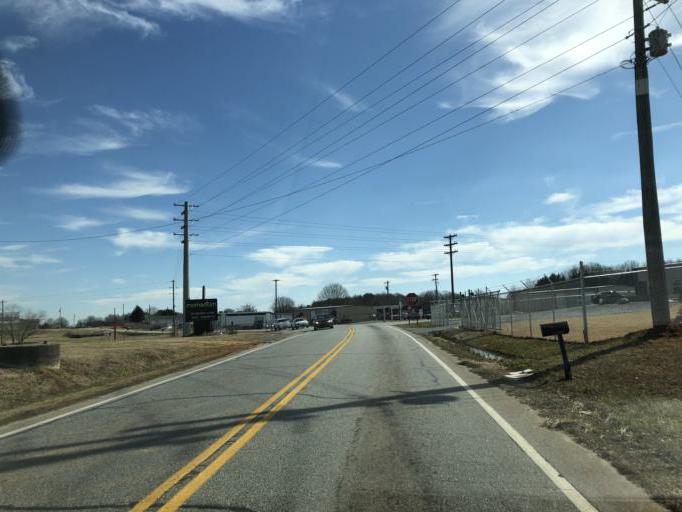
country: US
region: South Carolina
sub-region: Spartanburg County
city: Boiling Springs
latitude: 35.0508
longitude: -81.9271
